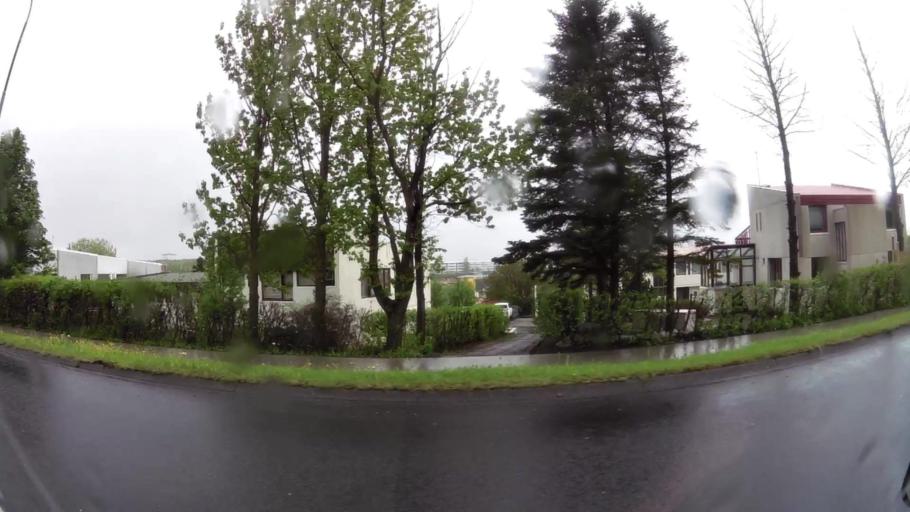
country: IS
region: Capital Region
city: Reykjavik
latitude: 64.1010
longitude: -21.8424
